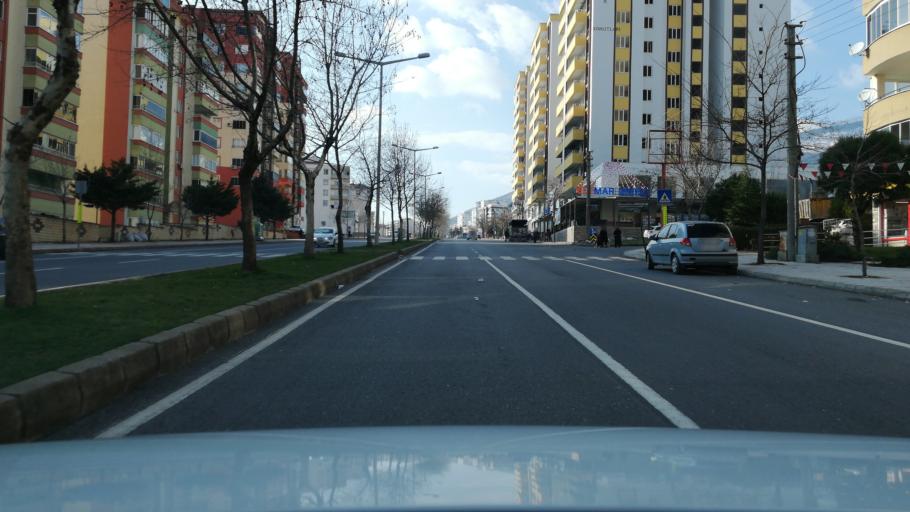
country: TR
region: Kahramanmaras
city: Kahramanmaras
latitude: 37.5938
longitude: 36.8953
